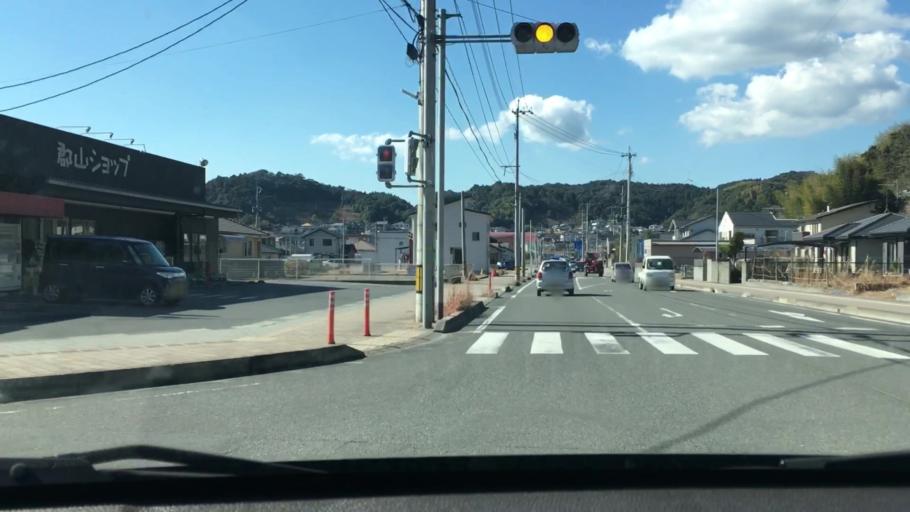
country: JP
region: Kagoshima
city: Ijuin
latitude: 31.6804
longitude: 130.4736
